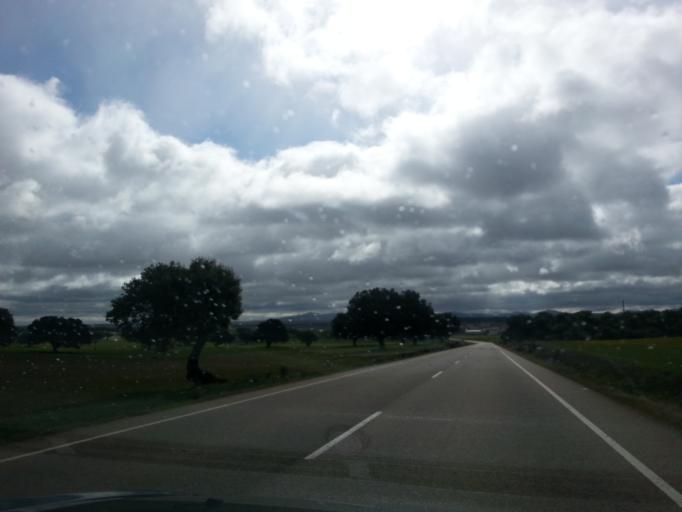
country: ES
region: Castille and Leon
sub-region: Provincia de Salamanca
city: Cabrillas
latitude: 40.7513
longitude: -6.1854
